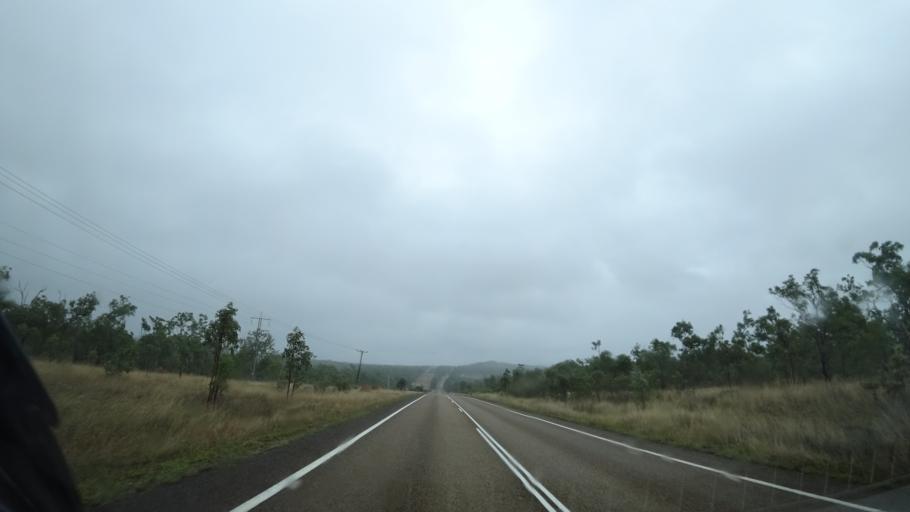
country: AU
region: Queensland
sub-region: Tablelands
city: Ravenshoe
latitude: -17.6985
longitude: 145.2039
